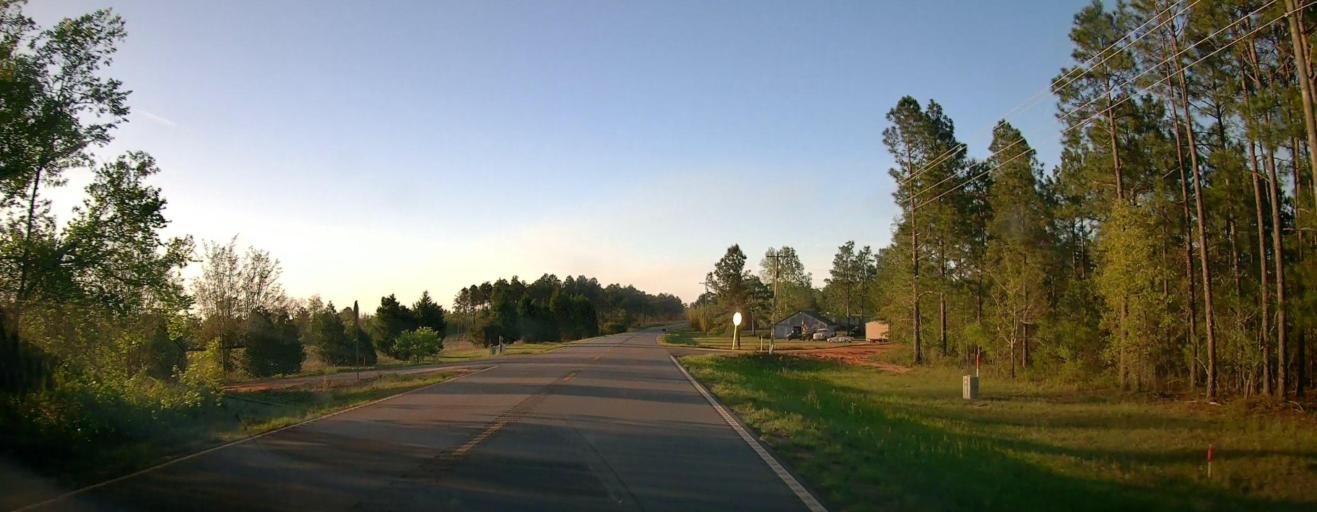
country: US
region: Georgia
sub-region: Talbot County
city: Talbotton
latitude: 32.5077
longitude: -84.4672
